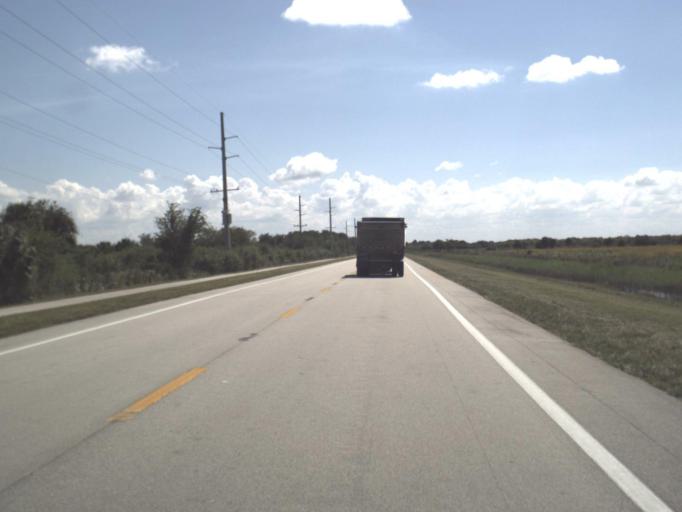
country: US
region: Florida
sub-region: Glades County
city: Moore Haven
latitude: 26.9413
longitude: -81.1222
